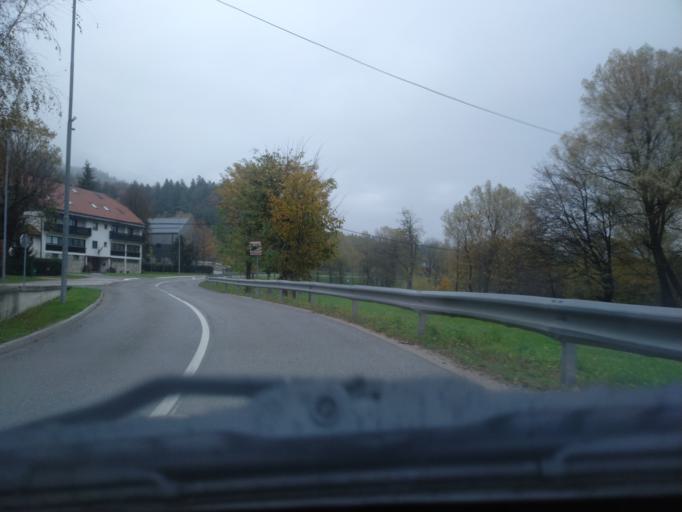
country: SI
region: Gornji Grad
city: Gornji Grad
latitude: 46.2972
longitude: 14.8103
